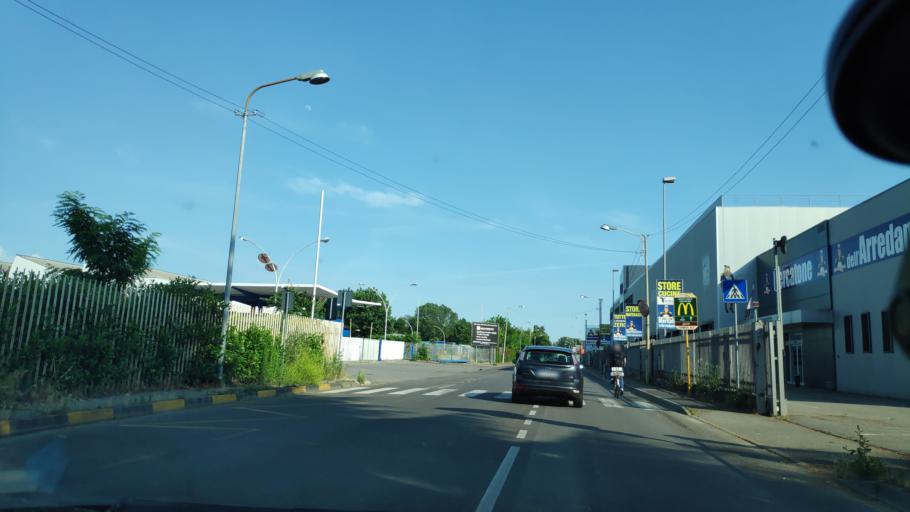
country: IT
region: Lombardy
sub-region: Citta metropolitana di Milano
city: Fizzonasco
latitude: 45.3762
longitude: 9.1850
